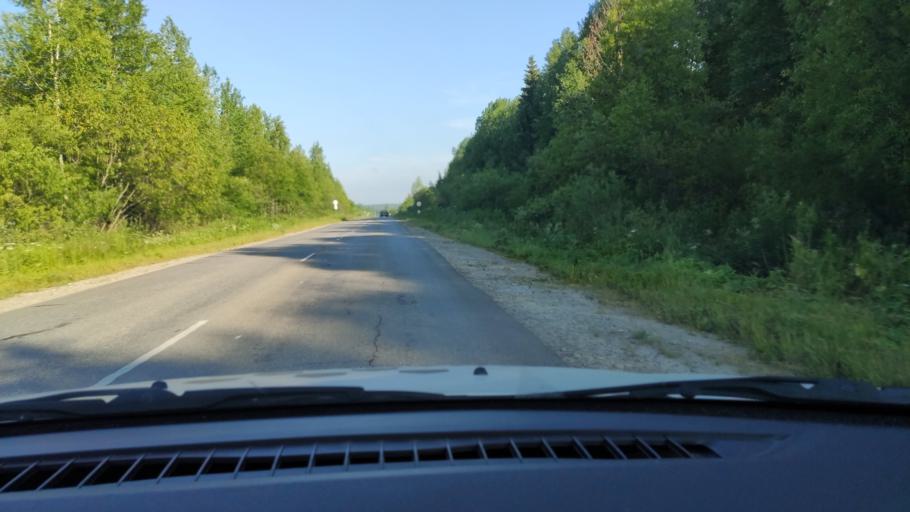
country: RU
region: Perm
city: Novyye Lyady
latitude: 58.0293
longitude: 56.6225
